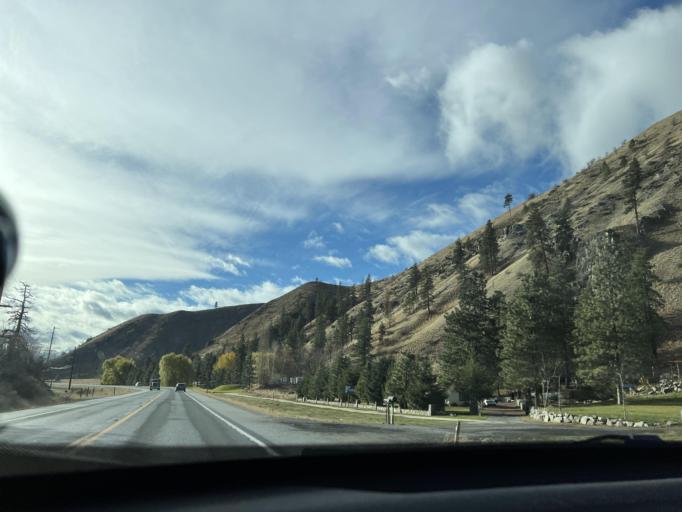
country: US
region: Washington
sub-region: Chelan County
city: Manson
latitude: 47.8128
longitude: -120.1323
